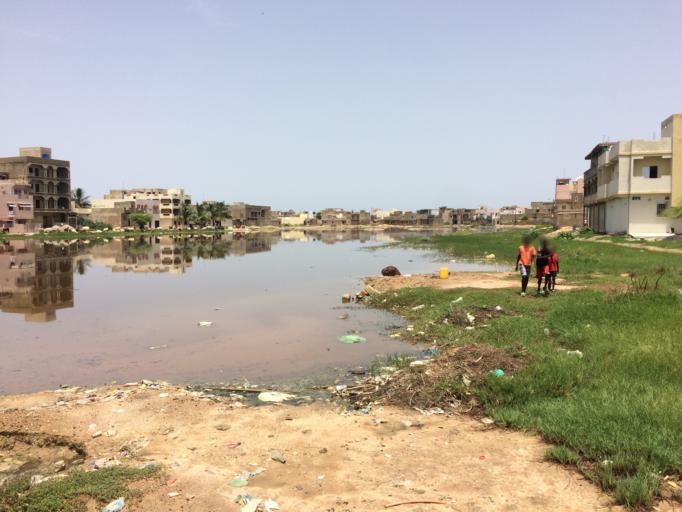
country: SN
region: Dakar
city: Pikine
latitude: 14.7344
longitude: -17.3290
